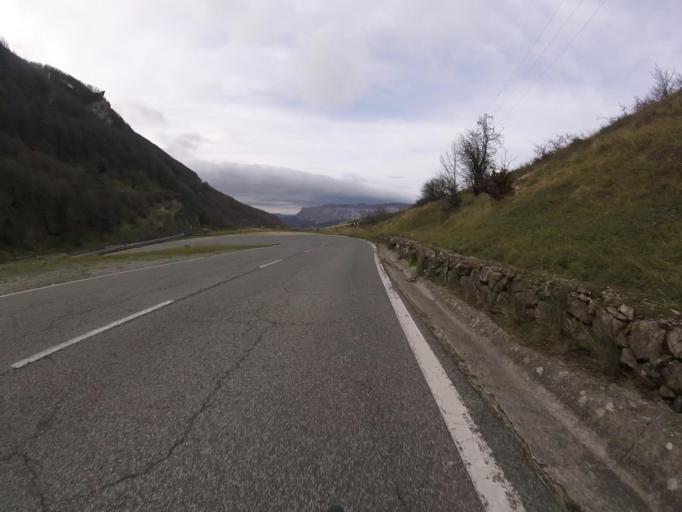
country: ES
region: Navarre
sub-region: Provincia de Navarra
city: Olazagutia
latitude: 42.8607
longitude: -2.1840
